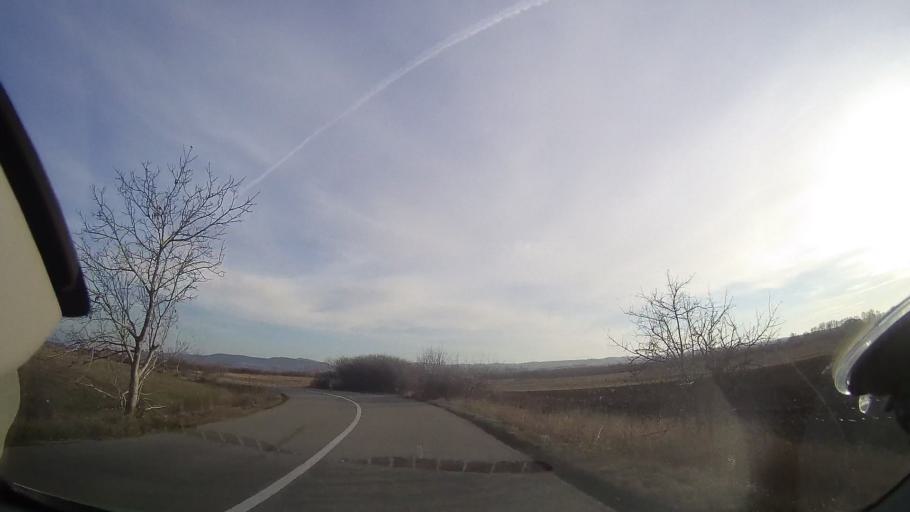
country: RO
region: Bihor
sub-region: Comuna Tileagd
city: Tileagd
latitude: 47.0581
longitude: 22.2493
